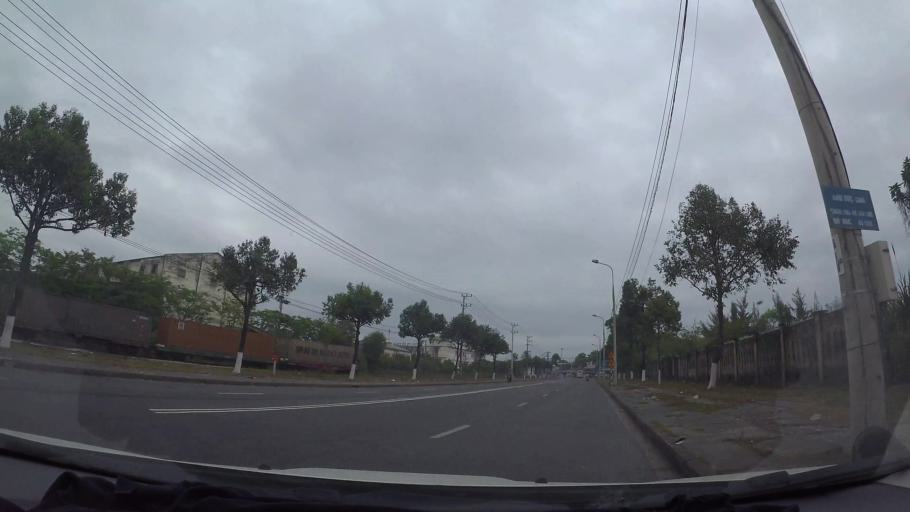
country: VN
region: Da Nang
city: Lien Chieu
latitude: 16.1277
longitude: 108.1176
